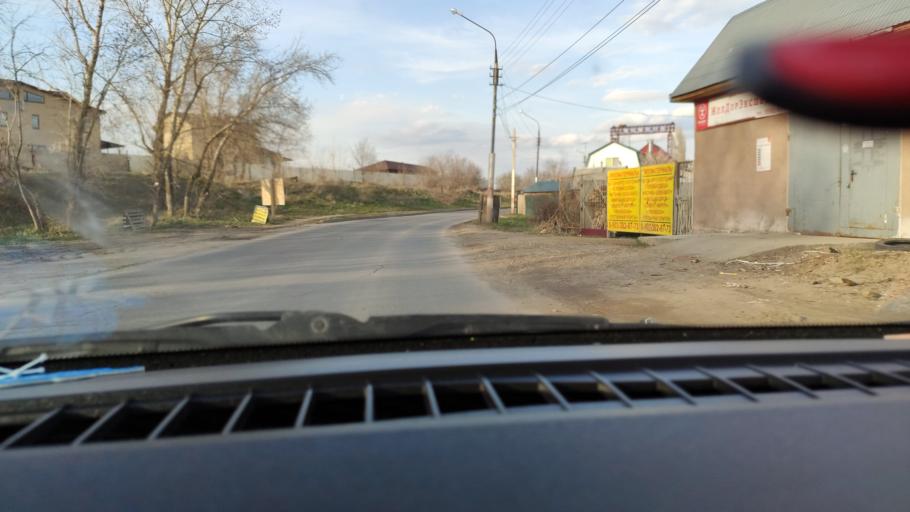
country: RU
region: Saratov
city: Engel's
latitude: 51.5034
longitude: 46.0713
